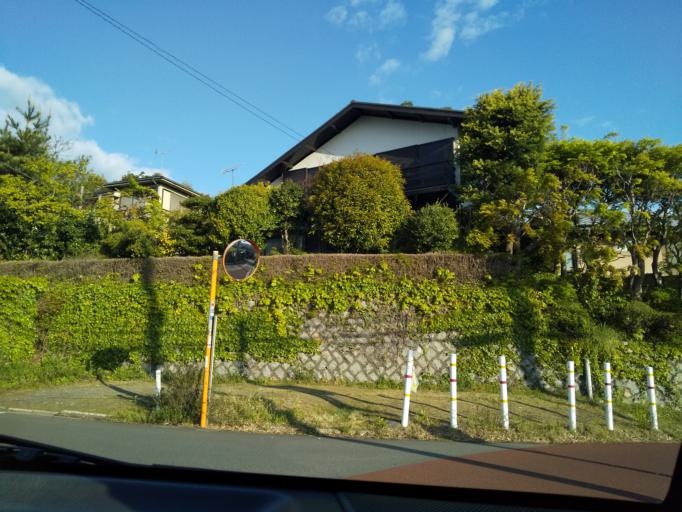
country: JP
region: Tokyo
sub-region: Machida-shi
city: Machida
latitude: 35.5688
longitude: 139.4583
